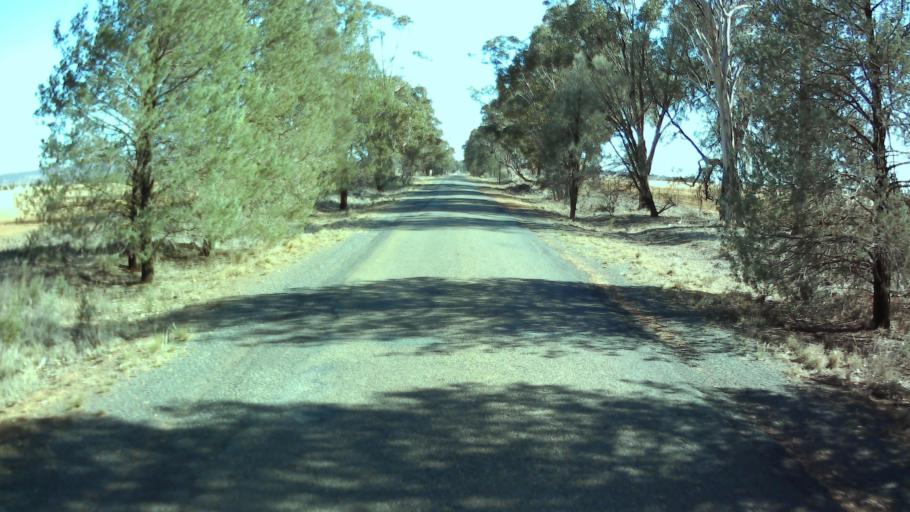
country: AU
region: New South Wales
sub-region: Weddin
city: Grenfell
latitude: -33.8048
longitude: 147.9551
